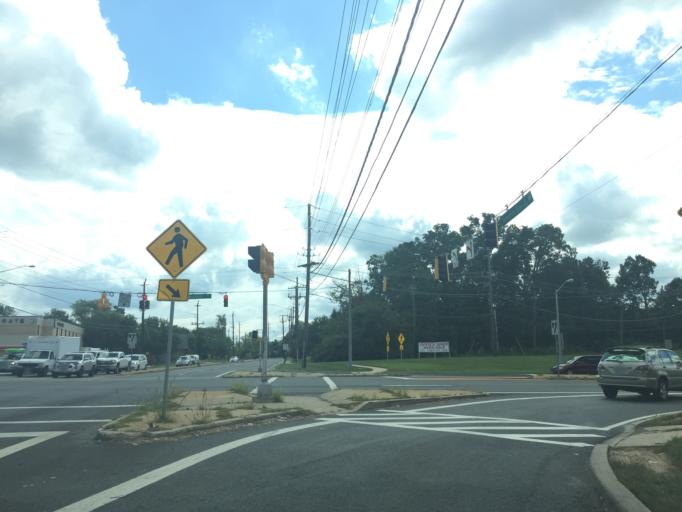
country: US
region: Maryland
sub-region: Montgomery County
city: Redland
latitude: 39.1592
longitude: -77.1607
